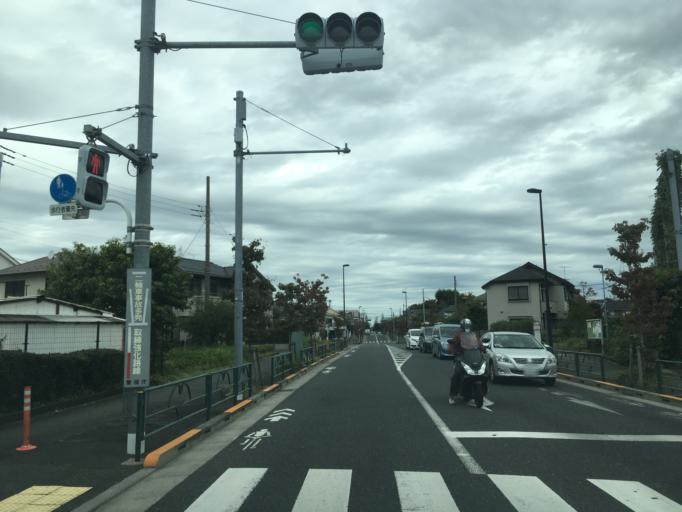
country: JP
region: Tokyo
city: Chofugaoka
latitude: 35.6302
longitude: 139.5713
